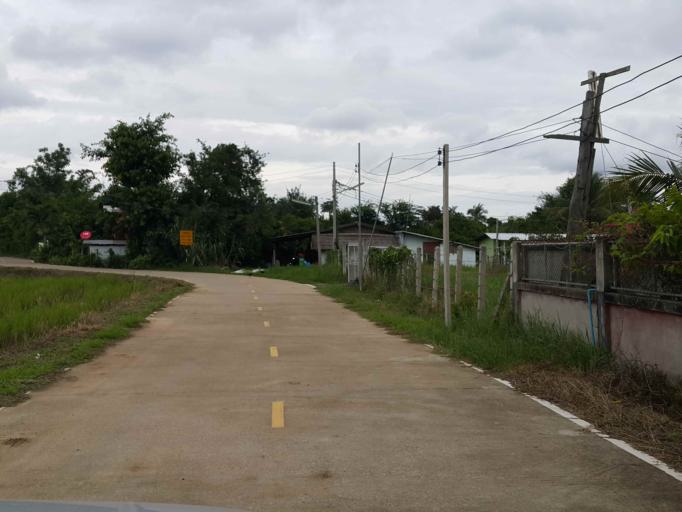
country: TH
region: Chiang Mai
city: San Sai
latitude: 18.8233
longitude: 99.0681
